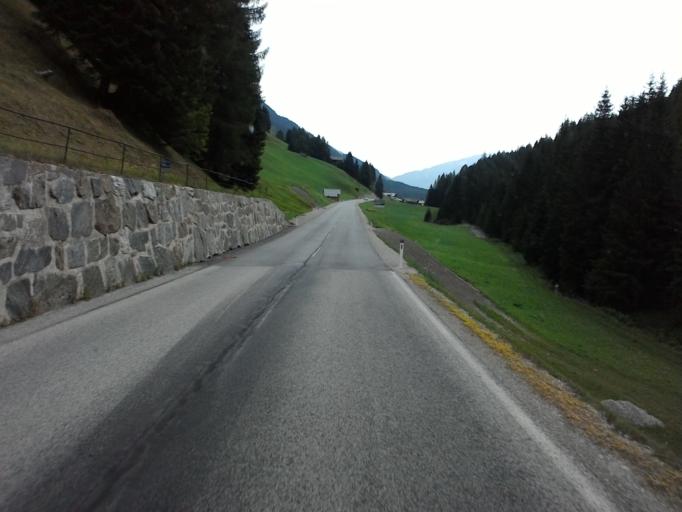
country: AT
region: Tyrol
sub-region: Politischer Bezirk Lienz
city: Abfaltersbach
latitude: 46.7165
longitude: 12.5499
